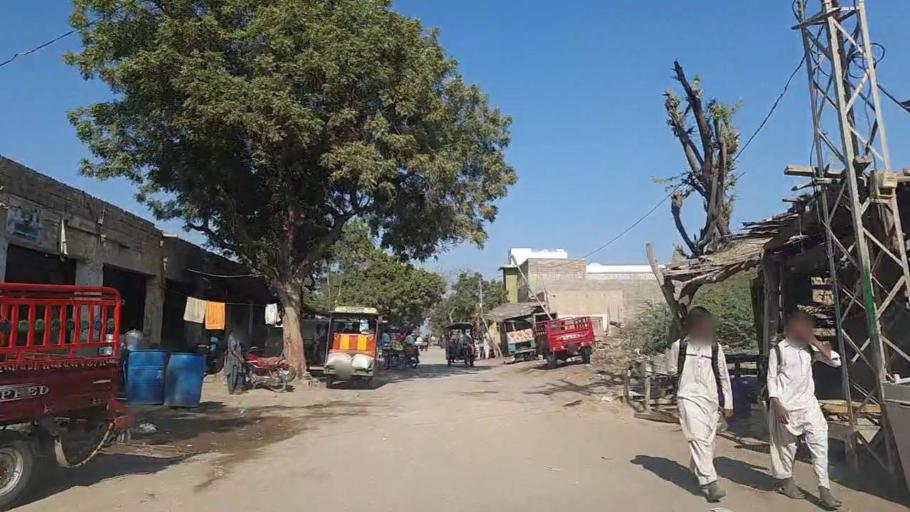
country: PK
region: Sindh
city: Digri
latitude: 25.0744
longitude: 69.2164
